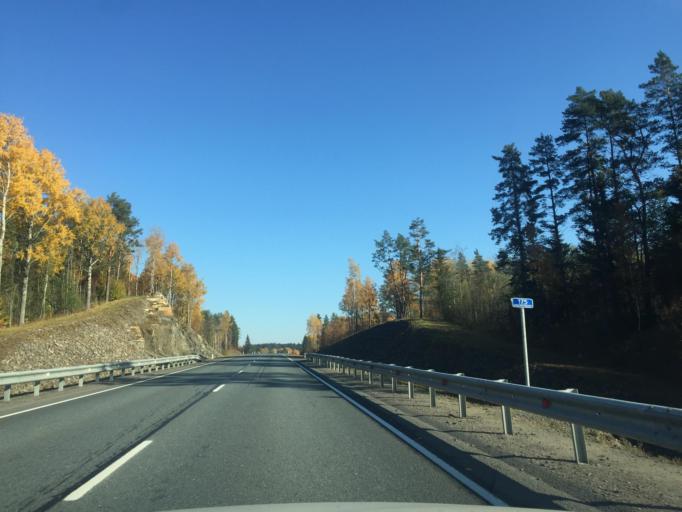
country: RU
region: Leningrad
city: Kuznechnoye
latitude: 61.3236
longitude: 29.8084
